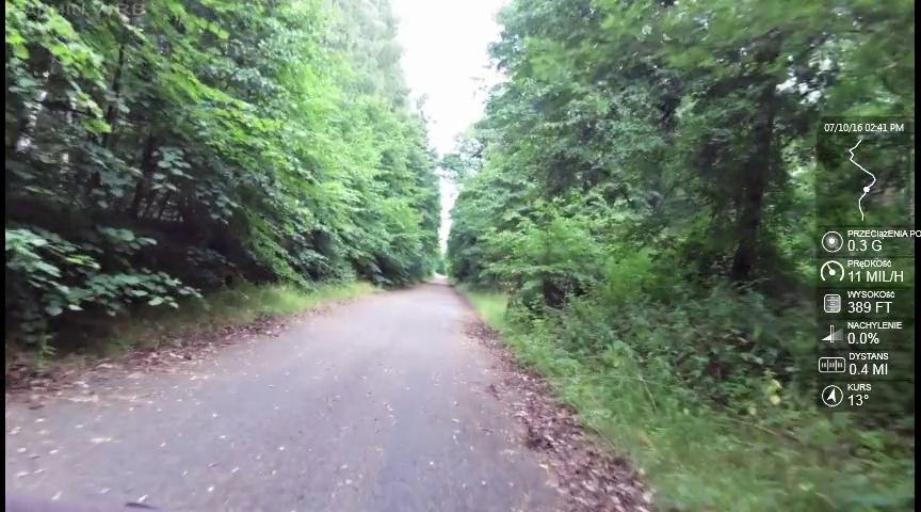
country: PL
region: West Pomeranian Voivodeship
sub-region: Powiat gryfinski
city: Banie
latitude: 53.0830
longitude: 14.6376
